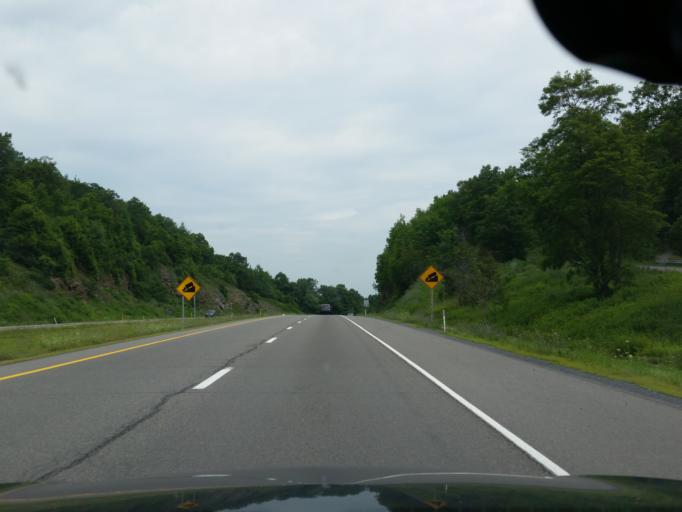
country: US
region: Pennsylvania
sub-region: Mifflin County
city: Milroy
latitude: 40.7657
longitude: -77.6158
